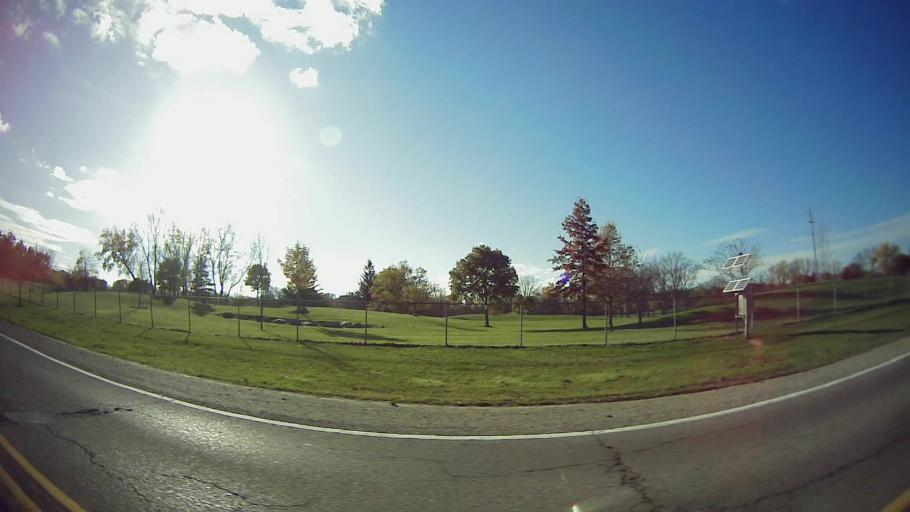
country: US
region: Michigan
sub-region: Oakland County
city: Beverly Hills
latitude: 42.5340
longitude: -83.2453
